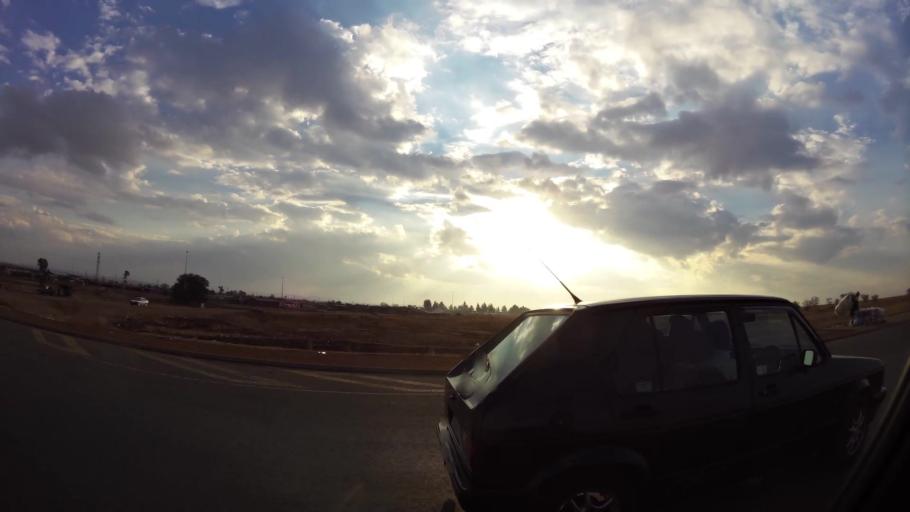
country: ZA
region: Gauteng
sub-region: Sedibeng District Municipality
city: Vanderbijlpark
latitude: -26.6013
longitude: 27.8183
